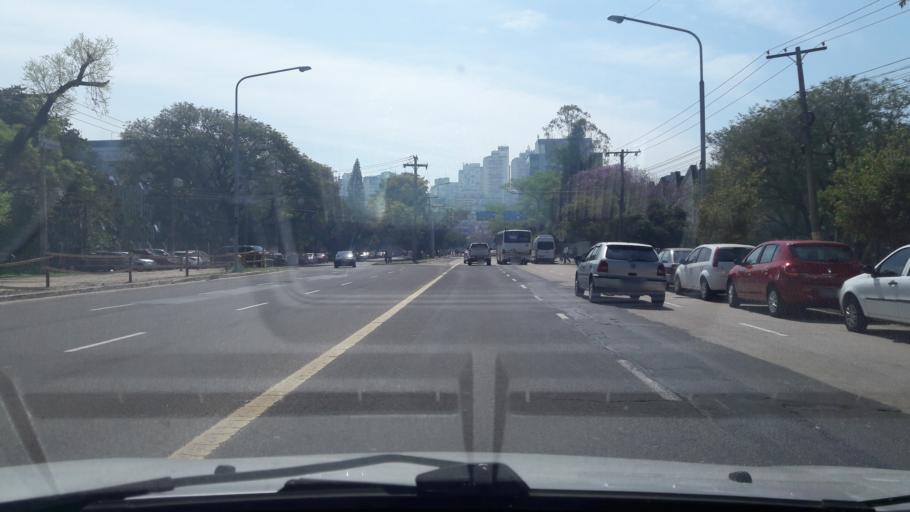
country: BR
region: Rio Grande do Sul
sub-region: Porto Alegre
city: Porto Alegre
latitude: -30.0394
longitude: -51.2328
